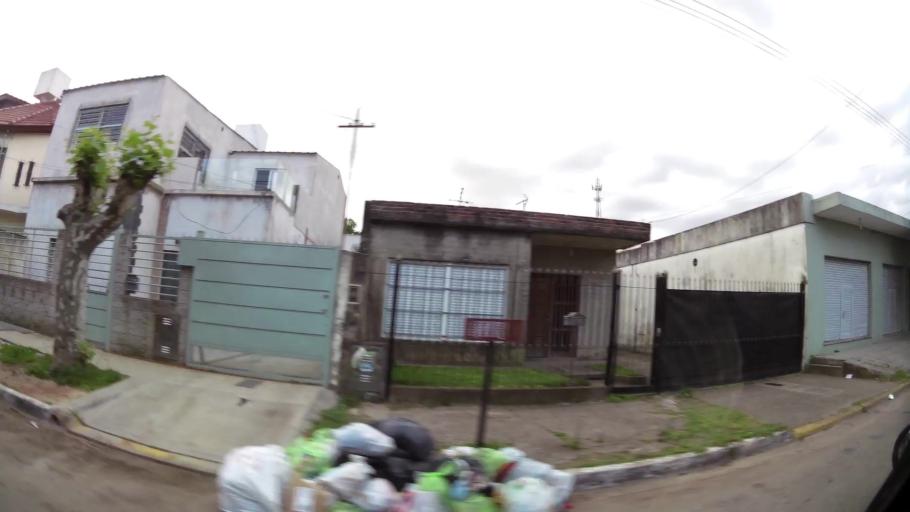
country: AR
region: Buenos Aires
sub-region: Partido de Quilmes
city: Quilmes
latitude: -34.7463
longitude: -58.2307
